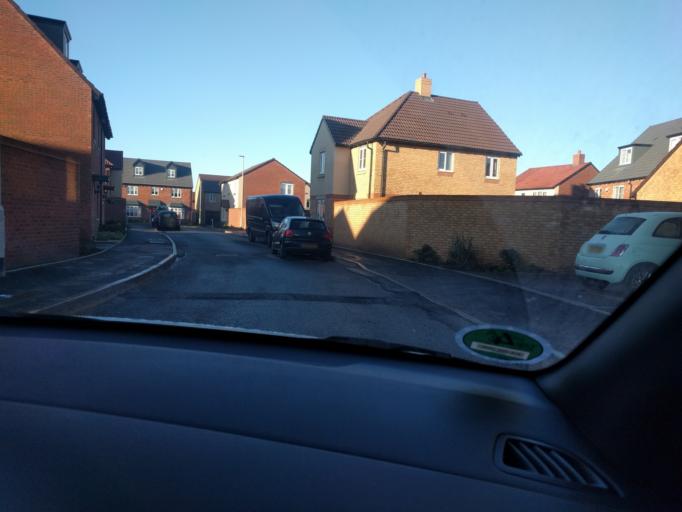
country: GB
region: England
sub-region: Telford and Wrekin
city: Wellington
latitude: 52.6933
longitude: -2.5144
